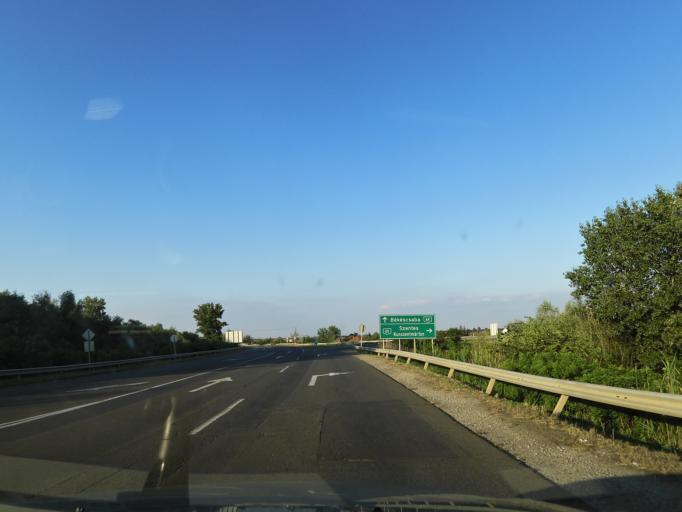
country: HU
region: Jasz-Nagykun-Szolnok
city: Kunszentmarton
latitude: 46.8492
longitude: 20.2773
